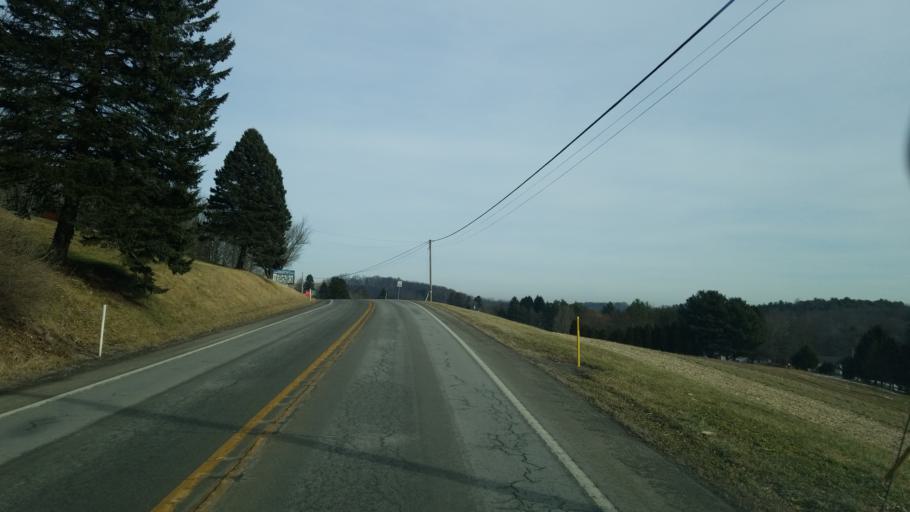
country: US
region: Pennsylvania
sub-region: Indiana County
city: Johnsonburg
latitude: 40.7488
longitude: -78.8898
